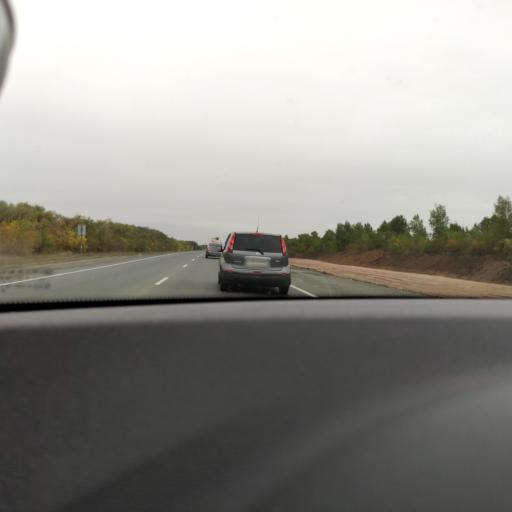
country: RU
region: Samara
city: Krasnyy Yar
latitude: 53.4617
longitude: 50.3935
